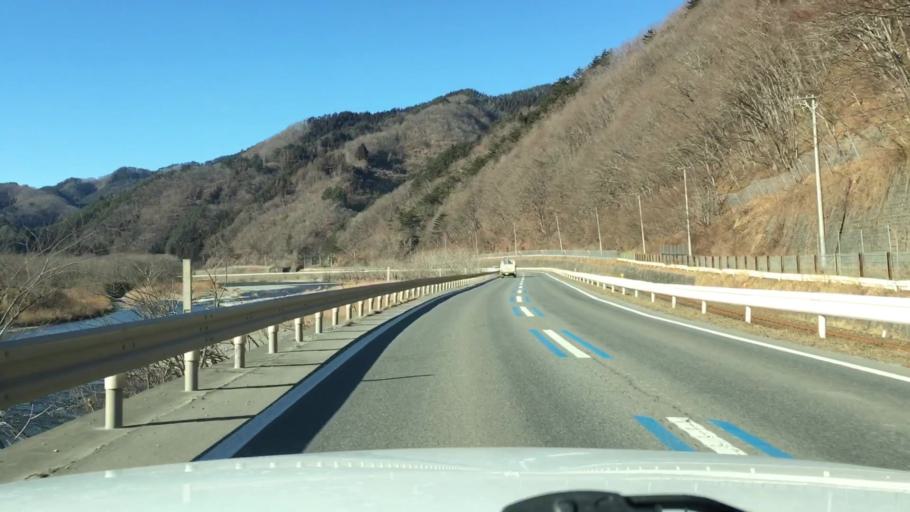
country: JP
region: Iwate
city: Miyako
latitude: 39.6309
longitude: 141.8540
